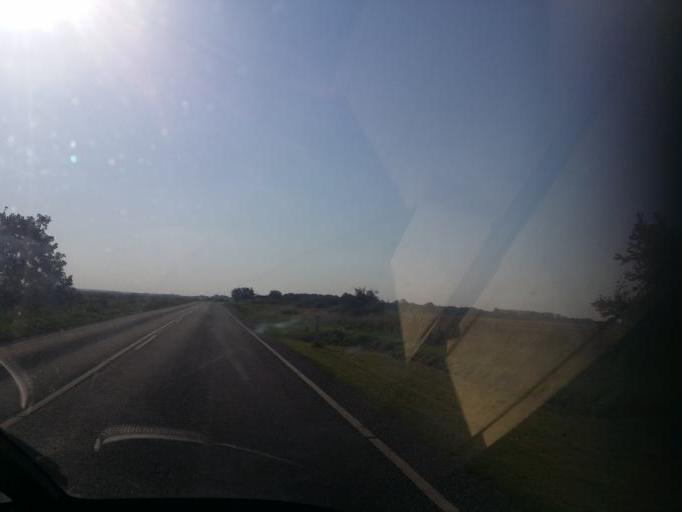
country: DE
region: Schleswig-Holstein
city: Neukirchen
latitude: 54.9121
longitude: 8.7430
